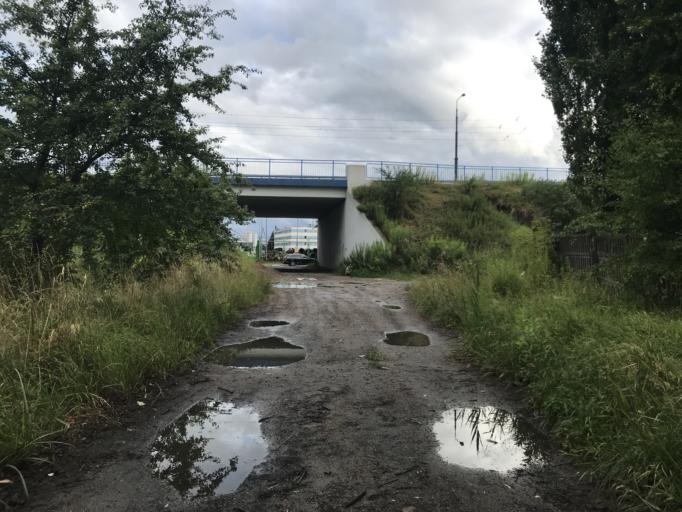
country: PL
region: Pomeranian Voivodeship
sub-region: Gdansk
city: Gdansk
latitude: 54.3539
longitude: 18.6760
